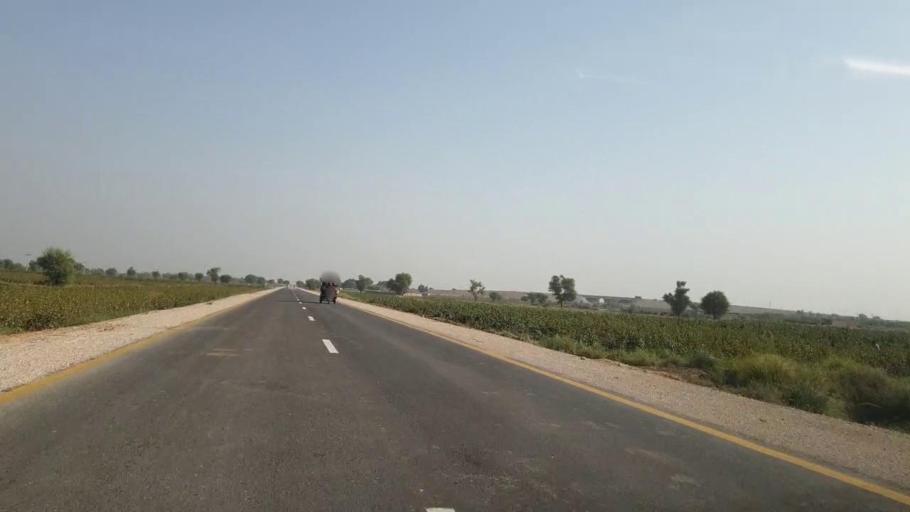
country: PK
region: Sindh
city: Sehwan
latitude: 26.4619
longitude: 67.8014
